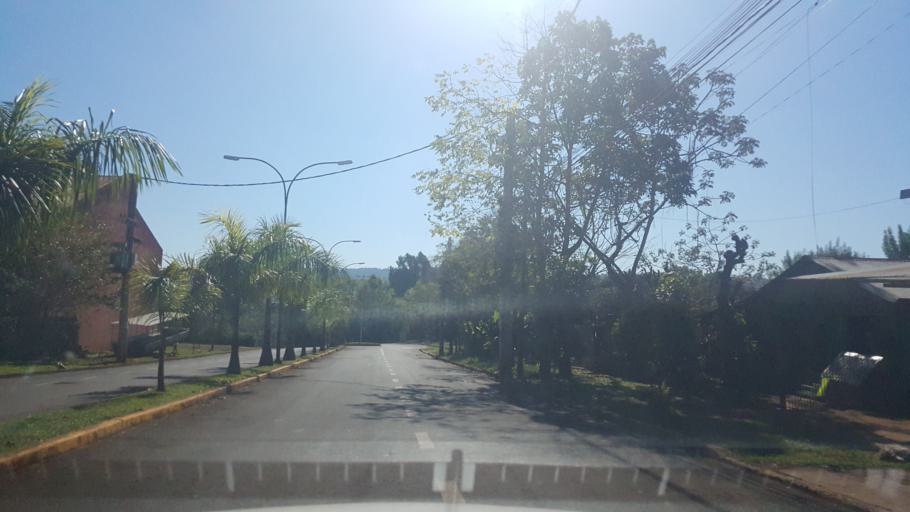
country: AR
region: Misiones
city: Puerto Rico
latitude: -26.7943
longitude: -55.0243
